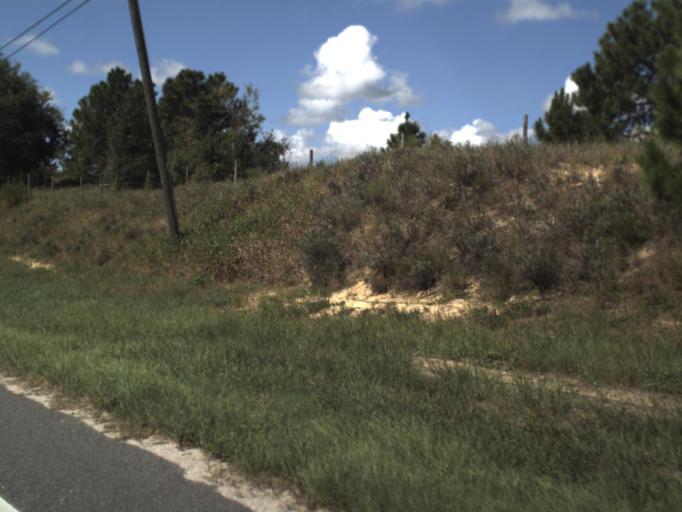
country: US
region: Florida
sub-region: Polk County
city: Davenport
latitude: 28.1964
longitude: -81.5841
